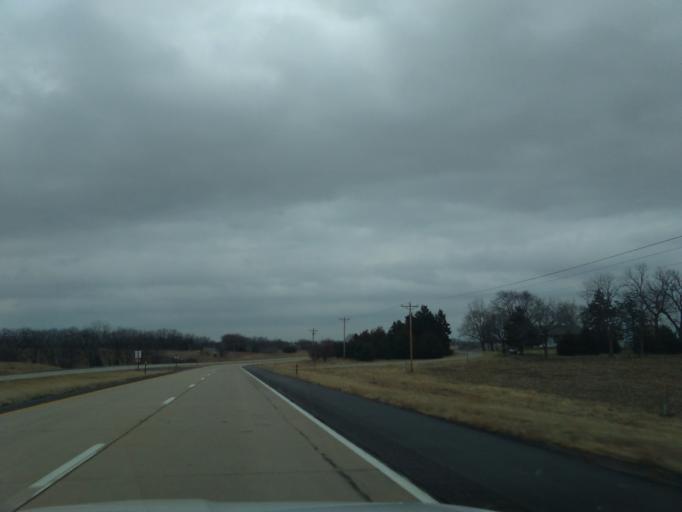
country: US
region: Nebraska
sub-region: Otoe County
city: Syracuse
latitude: 40.7114
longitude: -96.3083
